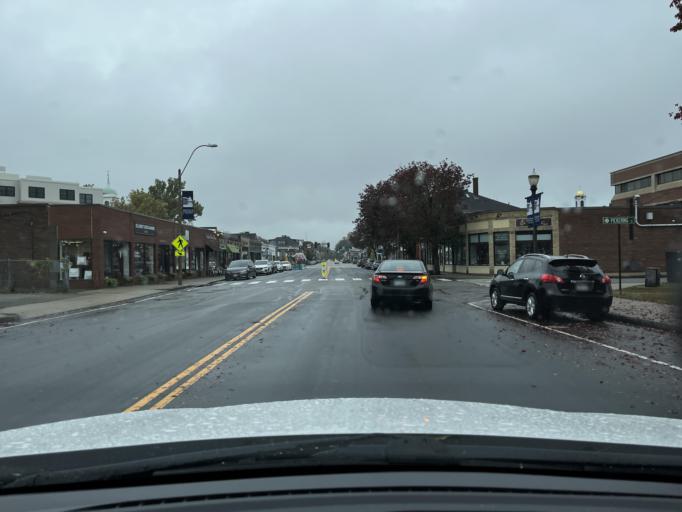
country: US
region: Massachusetts
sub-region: Norfolk County
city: Needham
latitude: 42.2803
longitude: -71.2341
